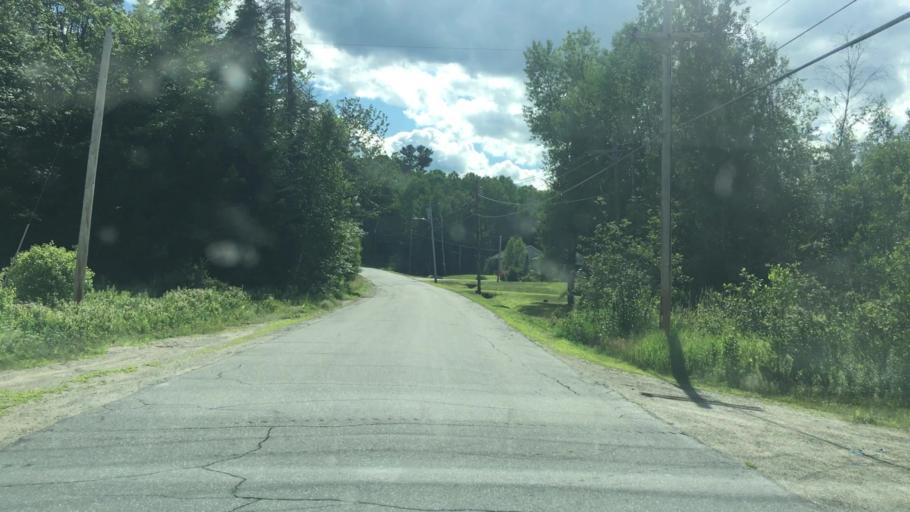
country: US
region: Maine
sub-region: Franklin County
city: Farmington
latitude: 44.6686
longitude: -70.1288
